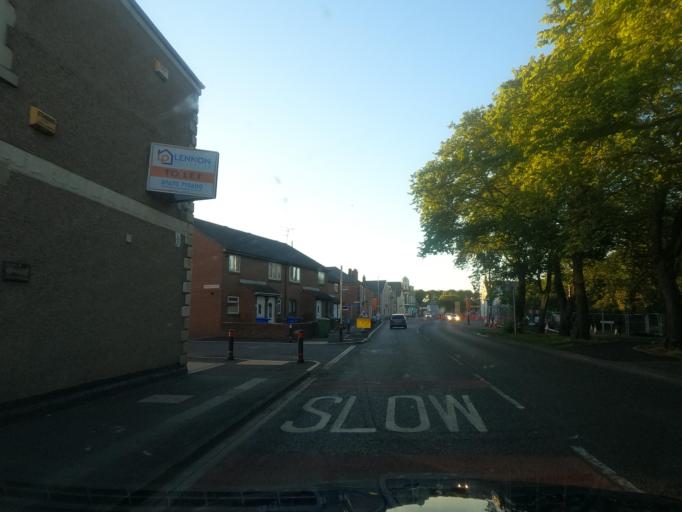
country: GB
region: England
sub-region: Northumberland
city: Blyth
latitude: 55.1248
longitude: -1.5164
